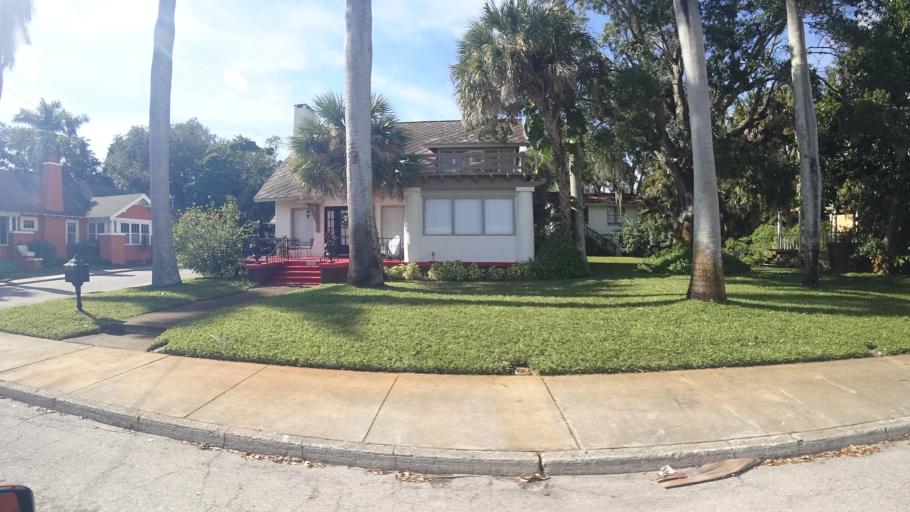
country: US
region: Florida
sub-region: Manatee County
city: Bradenton
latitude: 27.4948
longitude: -82.5785
